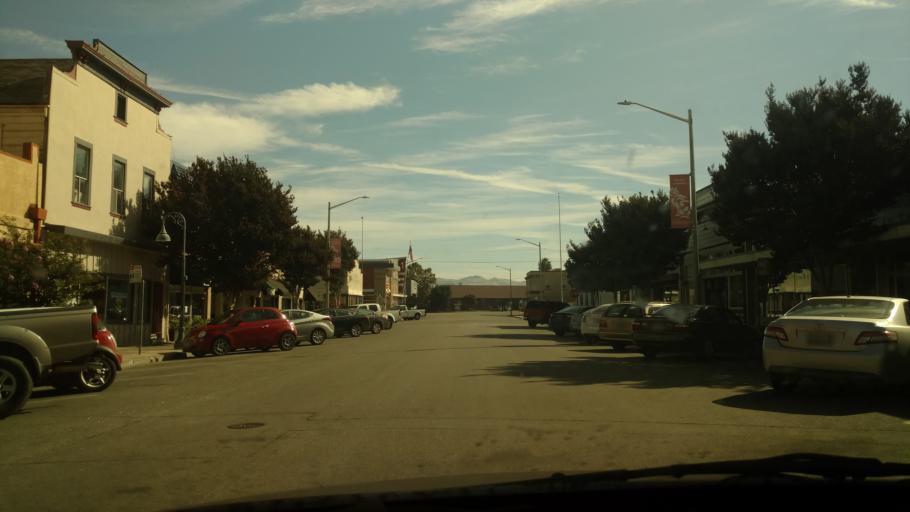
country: US
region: California
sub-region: San Benito County
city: Hollister
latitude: 36.8515
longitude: -121.4018
